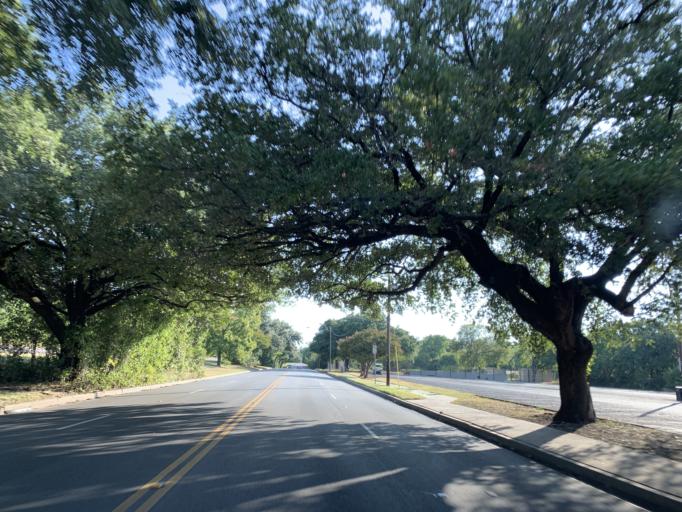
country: US
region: Texas
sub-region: Dallas County
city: Dallas
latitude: 32.7372
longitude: -96.8177
